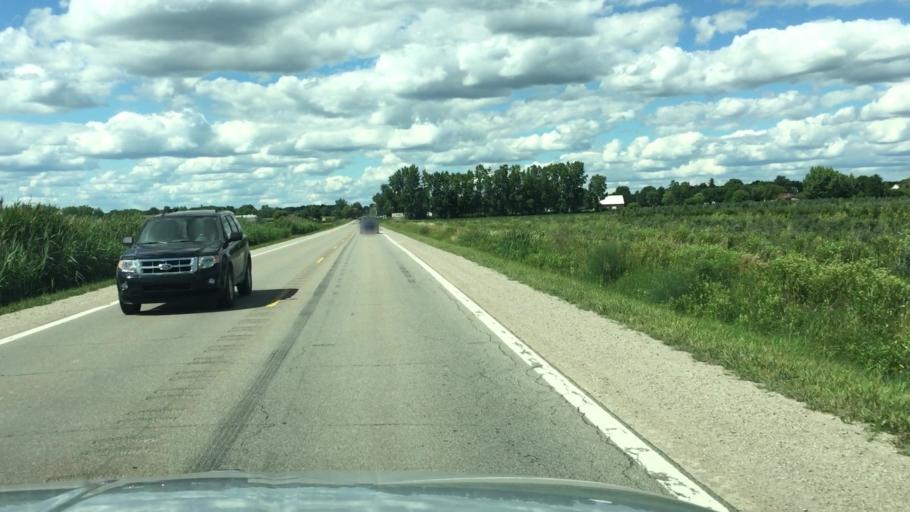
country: US
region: Michigan
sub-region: Macomb County
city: Romeo
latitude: 42.8430
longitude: -82.9641
